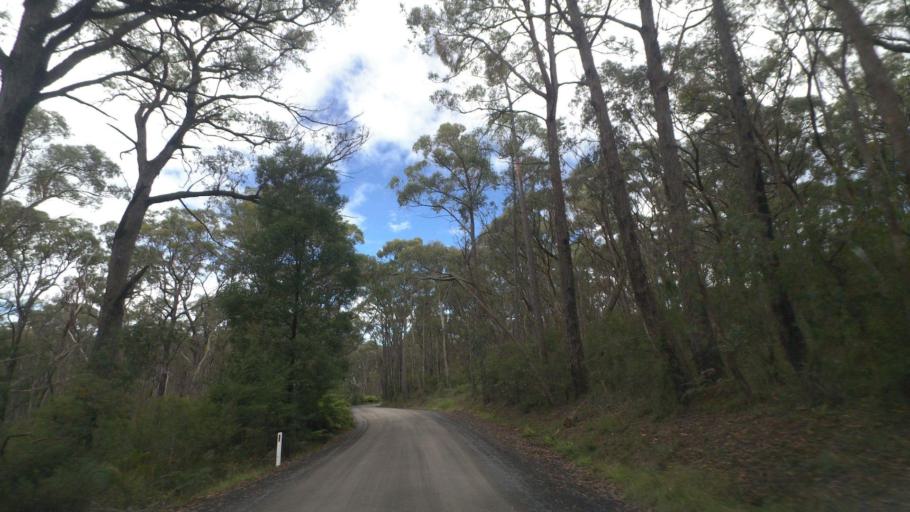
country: AU
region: Victoria
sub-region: Cardinia
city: Gembrook
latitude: -37.8886
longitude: 145.5876
